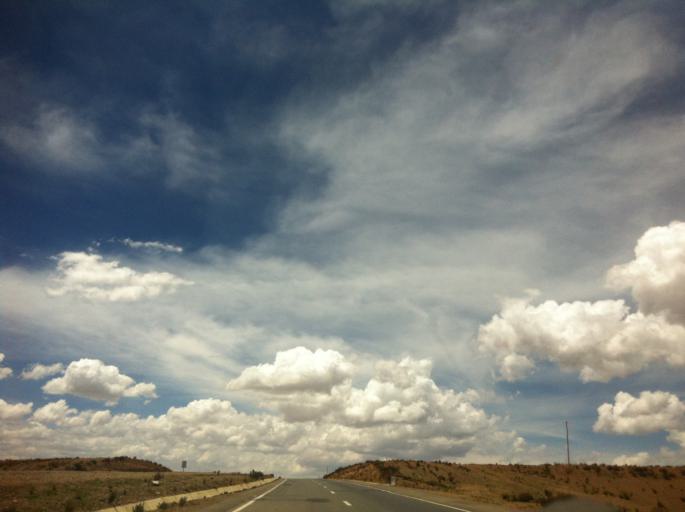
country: BO
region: La Paz
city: Patacamaya
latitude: -17.0877
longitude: -68.0123
